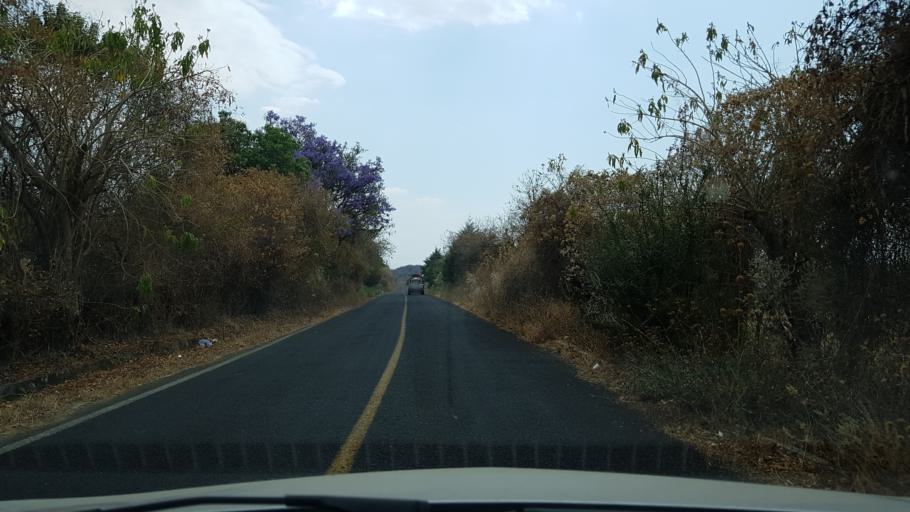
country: MX
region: Morelos
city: Tlacotepec
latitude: 18.8337
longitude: -98.7360
